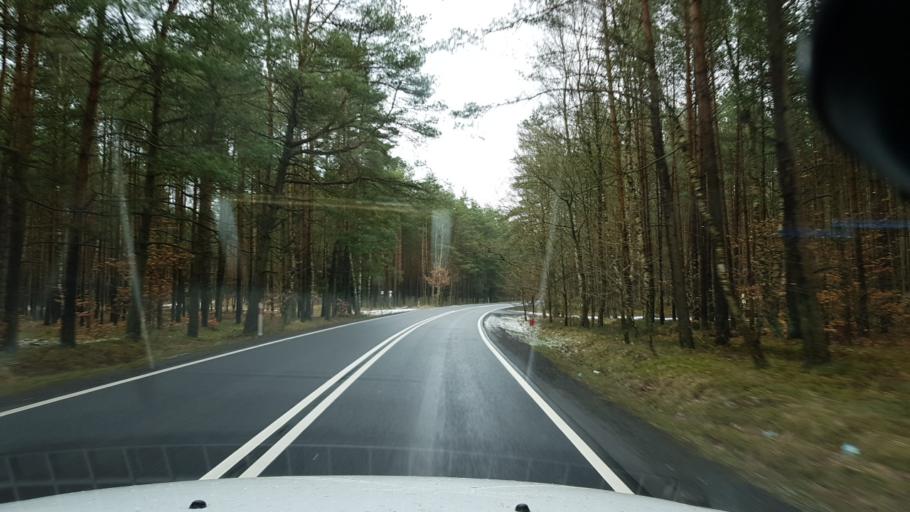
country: PL
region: West Pomeranian Voivodeship
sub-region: Powiat goleniowski
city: Stepnica
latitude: 53.6291
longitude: 14.7133
